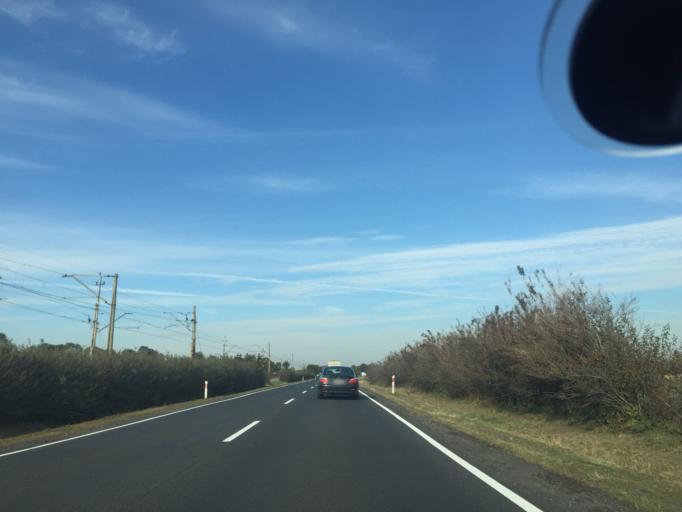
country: PL
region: Greater Poland Voivodeship
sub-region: Powiat gnieznienski
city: Trzemeszno
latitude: 52.5961
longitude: 17.8933
